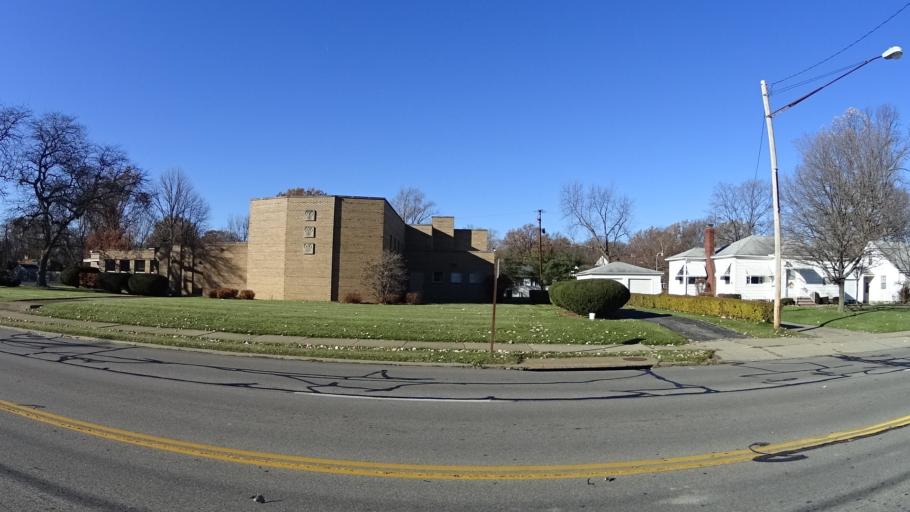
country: US
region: Ohio
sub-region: Lorain County
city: Elyria
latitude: 41.3807
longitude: -82.0943
